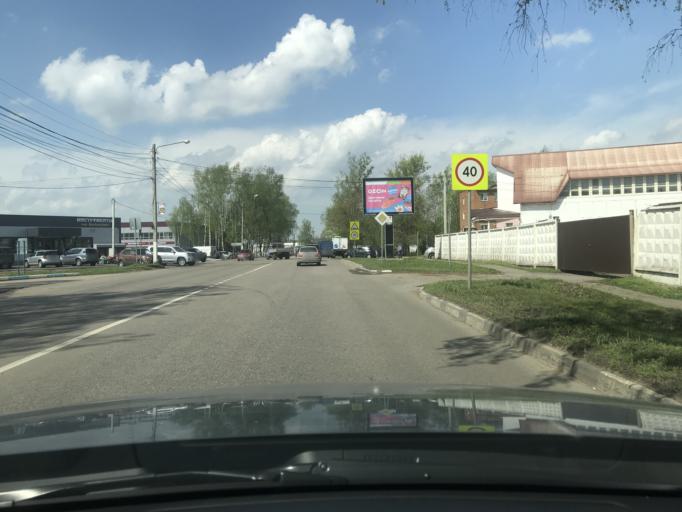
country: RU
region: Moskovskaya
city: Naro-Fominsk
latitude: 55.3761
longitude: 36.7660
